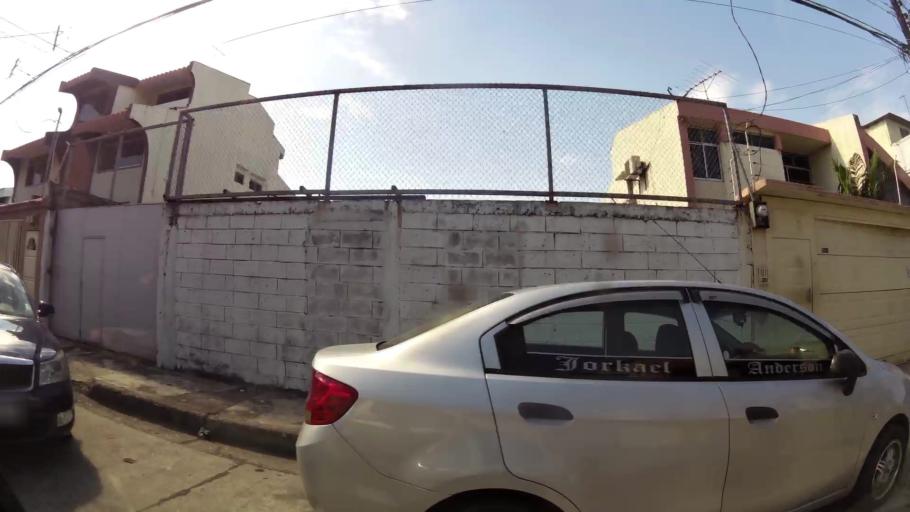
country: EC
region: Guayas
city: Guayaquil
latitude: -2.2251
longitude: -79.8961
